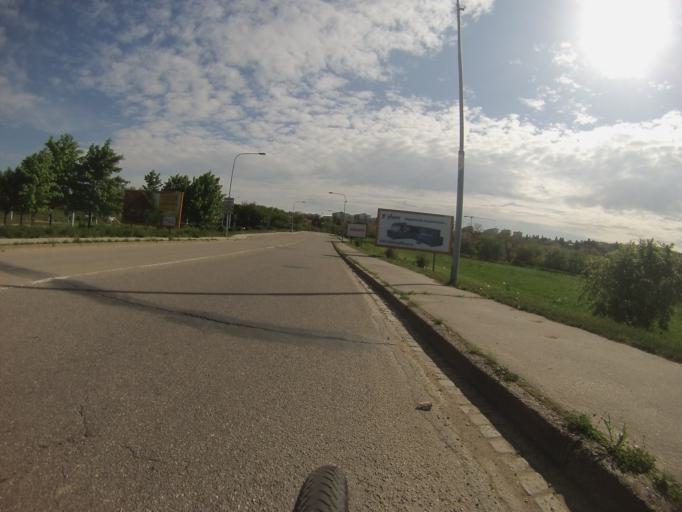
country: CZ
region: South Moravian
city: Troubsko
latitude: 49.2264
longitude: 16.5186
